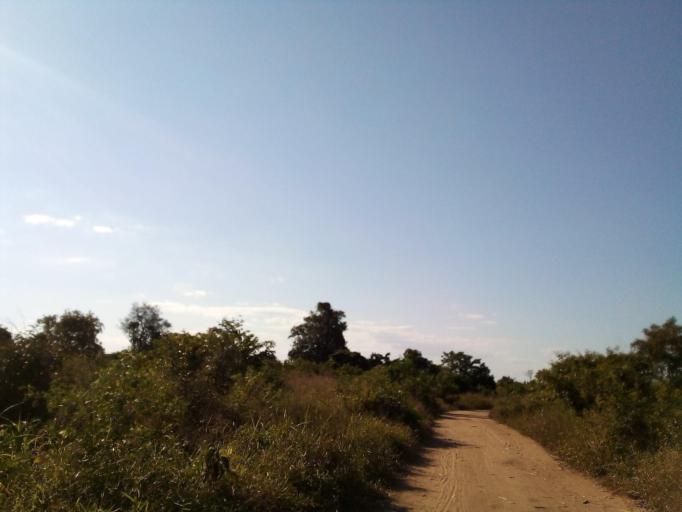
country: MZ
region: Zambezia
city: Quelimane
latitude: -17.5252
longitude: 36.6815
